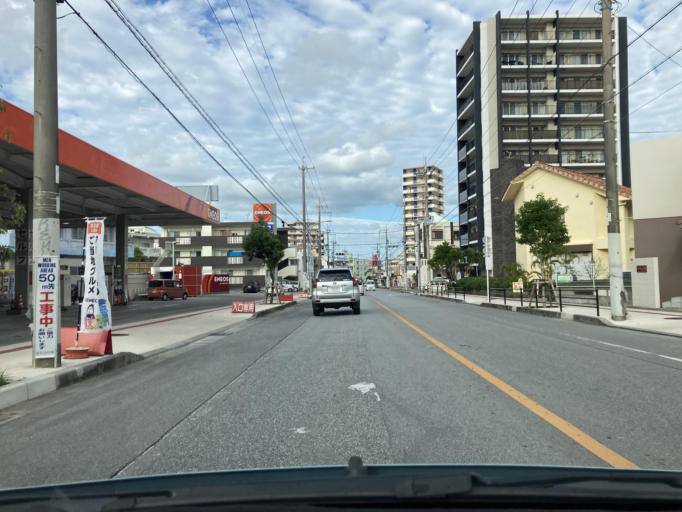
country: JP
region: Okinawa
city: Okinawa
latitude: 26.3396
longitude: 127.8217
